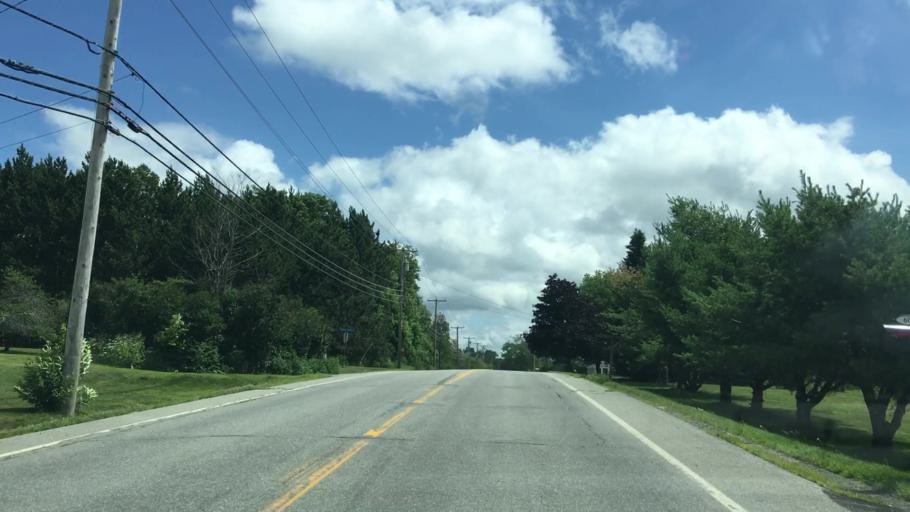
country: US
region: Maine
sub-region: Penobscot County
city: Carmel
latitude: 44.8032
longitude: -69.0284
